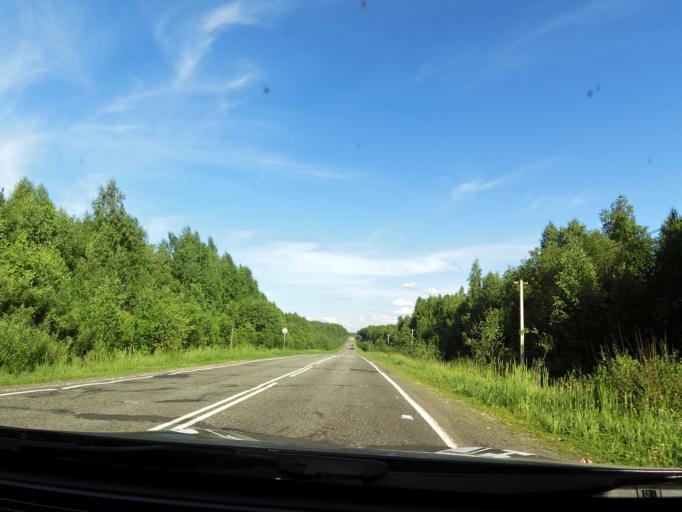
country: RU
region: Kirov
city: Belaya Kholunitsa
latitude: 58.9200
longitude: 51.1230
